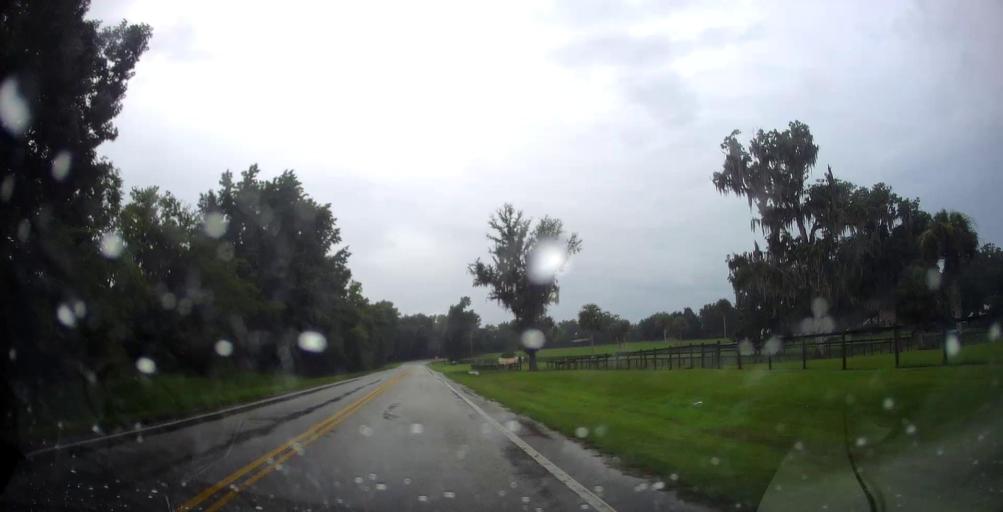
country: US
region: Florida
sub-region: Marion County
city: Citra
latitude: 29.3924
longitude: -82.2475
